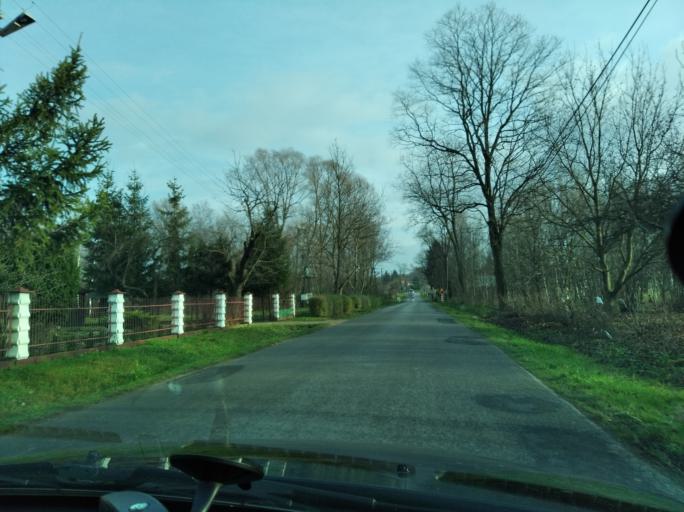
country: PL
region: Subcarpathian Voivodeship
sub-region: Powiat przeworski
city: Siedleczka
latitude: 49.9543
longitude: 22.3941
